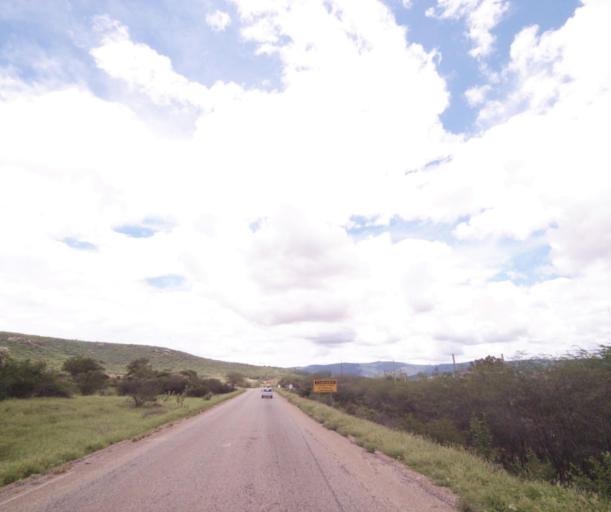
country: BR
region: Bahia
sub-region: Brumado
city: Brumado
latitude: -14.1992
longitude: -41.5985
